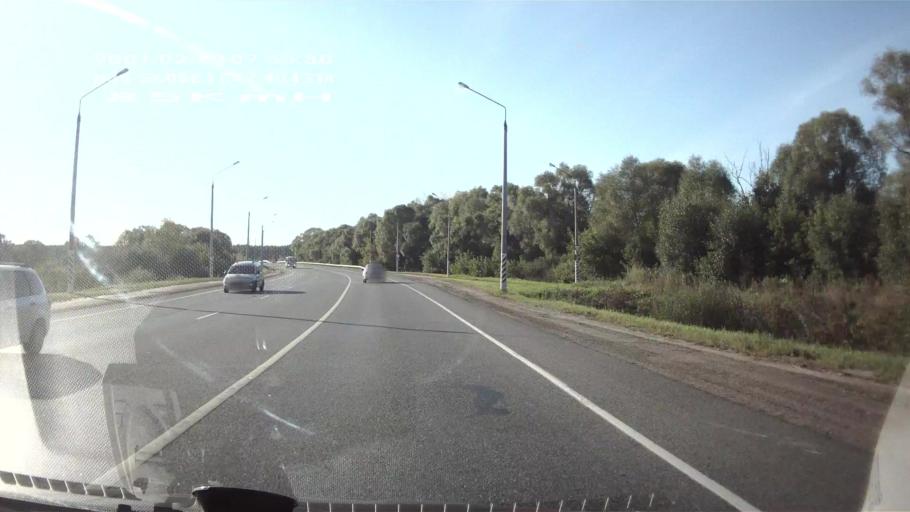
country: RU
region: Chuvashia
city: Shikhazany
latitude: 55.5607
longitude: 47.4046
